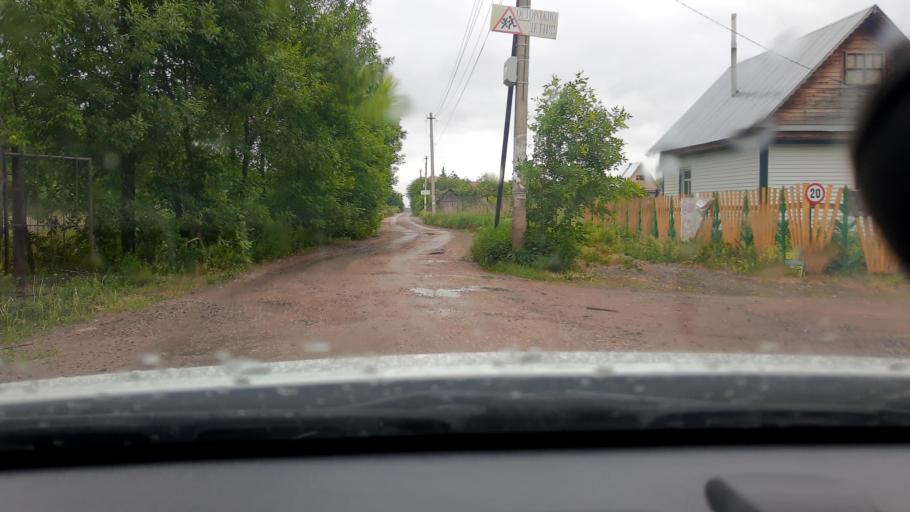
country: RU
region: Bashkortostan
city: Kabakovo
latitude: 54.4733
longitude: 55.9375
